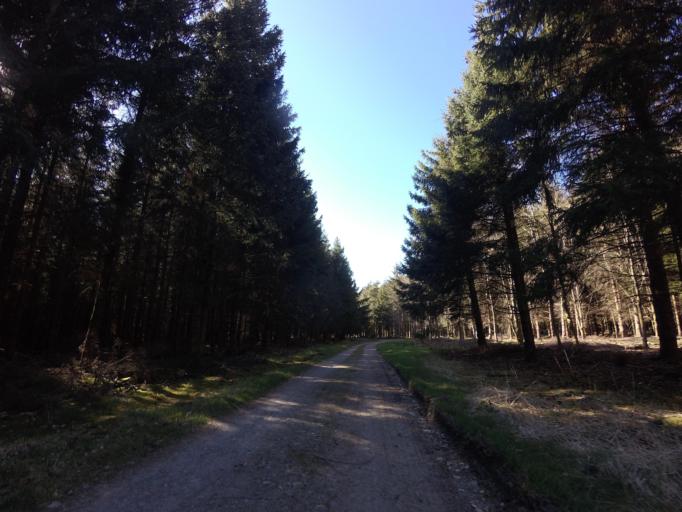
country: BE
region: Wallonia
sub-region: Province de Liege
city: Trois-Ponts
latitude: 50.4027
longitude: 5.8892
